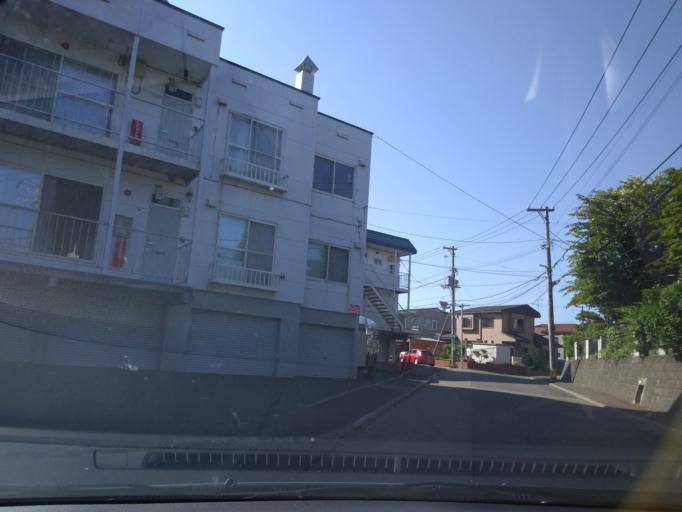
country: JP
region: Hokkaido
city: Sapporo
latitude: 43.0171
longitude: 141.4558
